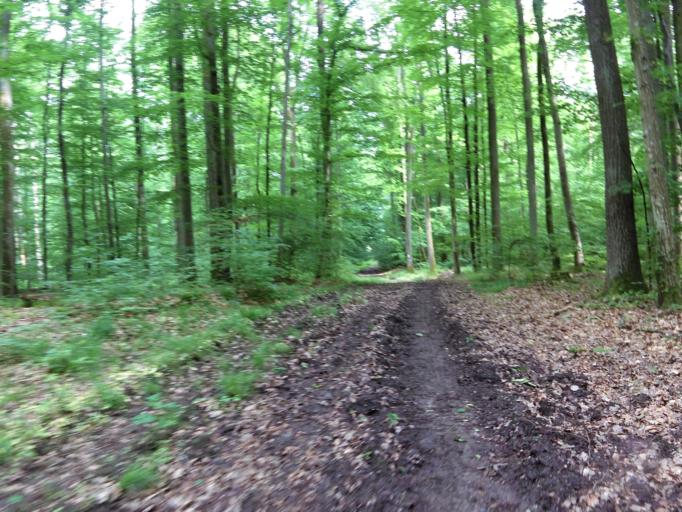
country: DE
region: Bavaria
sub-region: Regierungsbezirk Unterfranken
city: Kist
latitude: 49.7253
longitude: 9.8358
